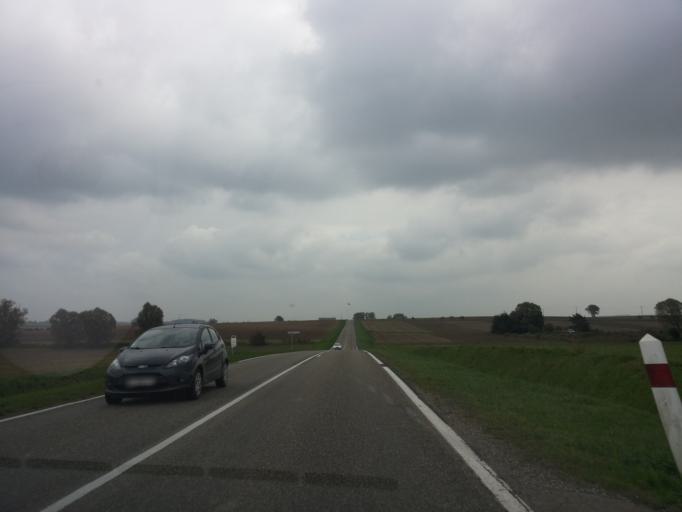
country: FR
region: Lorraine
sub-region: Departement de la Moselle
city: Vic-sur-Seille
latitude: 48.7624
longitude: 6.5931
